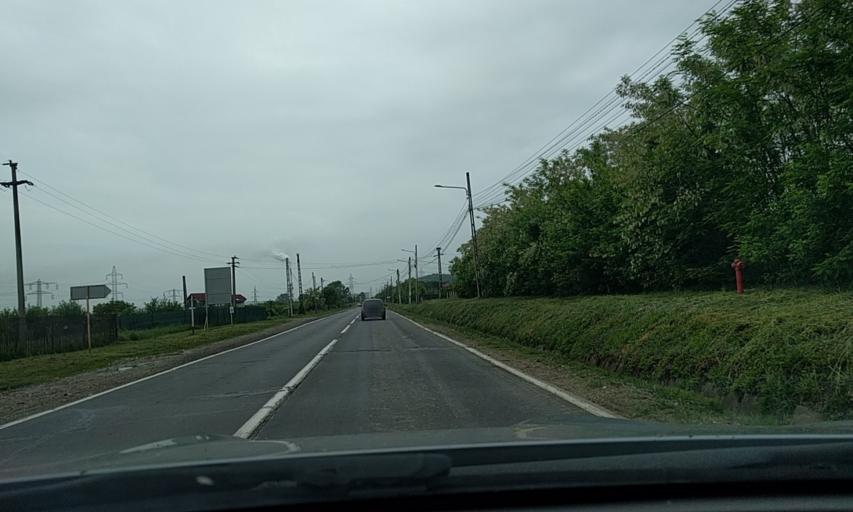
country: RO
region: Dambovita
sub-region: Comuna Aninoasa
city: Sateni
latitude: 44.9762
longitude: 25.4263
